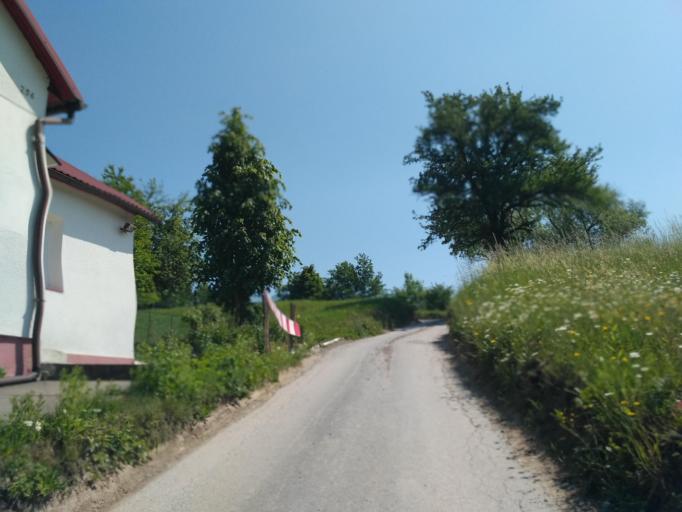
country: PL
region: Subcarpathian Voivodeship
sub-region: Powiat brzozowski
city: Golcowa
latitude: 49.8158
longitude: 22.0452
